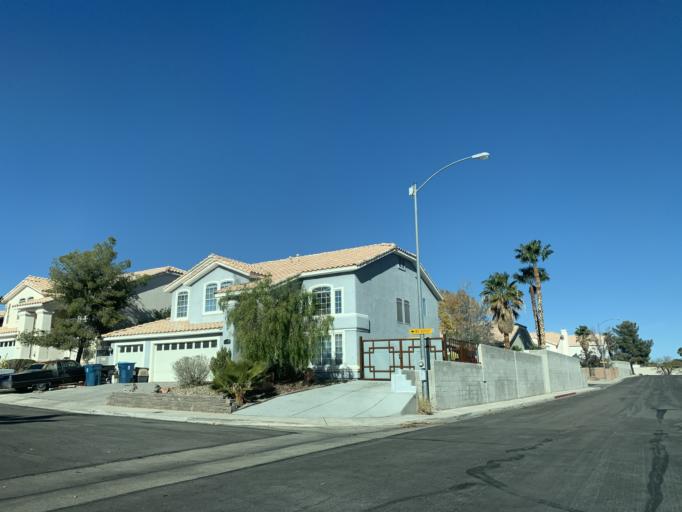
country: US
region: Nevada
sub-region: Clark County
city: Spring Valley
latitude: 36.1227
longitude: -115.2862
